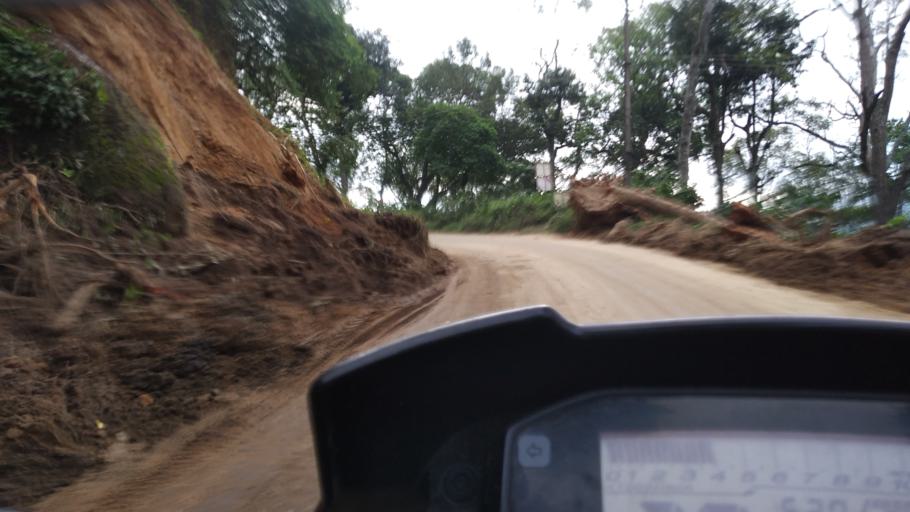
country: IN
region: Tamil Nadu
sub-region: Theni
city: Bodinayakkanur
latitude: 10.0192
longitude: 77.2454
